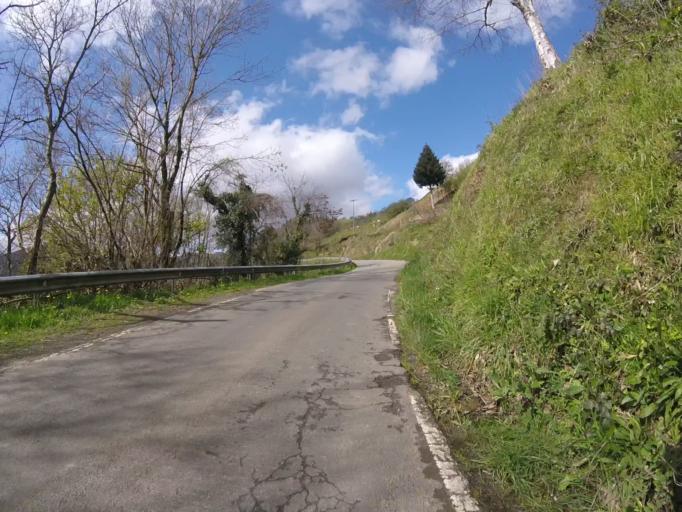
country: ES
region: Basque Country
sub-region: Provincia de Guipuzcoa
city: Tolosa
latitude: 43.1305
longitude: -2.1013
